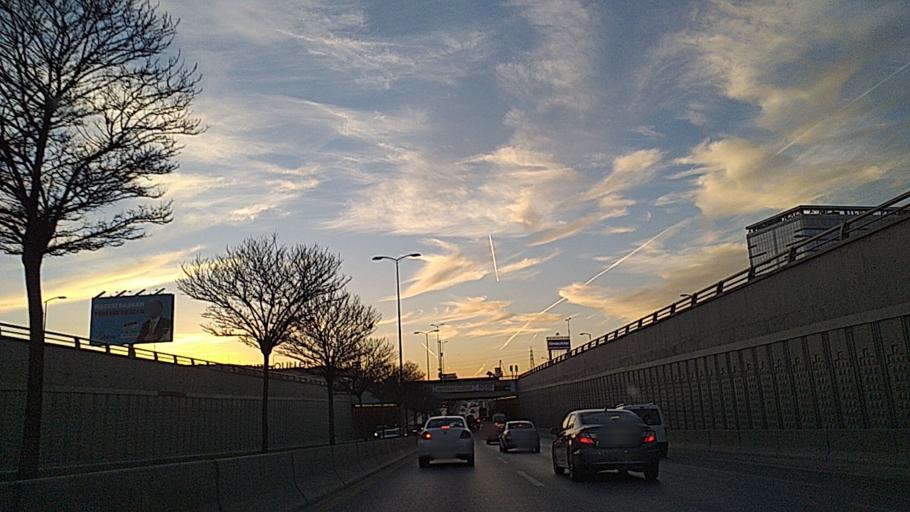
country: TR
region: Ankara
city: Etimesgut
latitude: 39.9654
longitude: 32.6379
